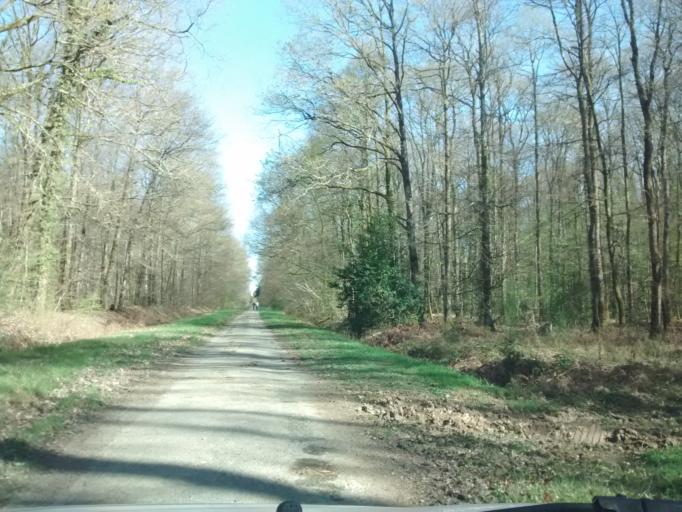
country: FR
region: Brittany
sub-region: Departement d'Ille-et-Vilaine
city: Chasne-sur-Illet
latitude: 48.2201
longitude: -1.5449
